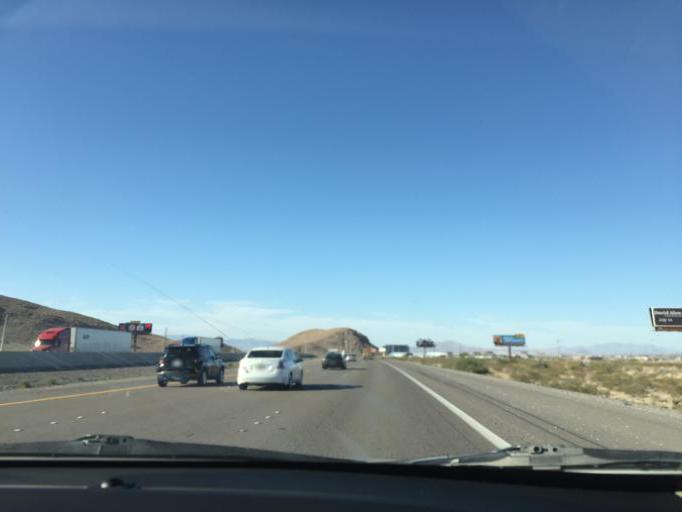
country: US
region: Nevada
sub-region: Clark County
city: Enterprise
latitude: 35.9408
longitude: -115.1857
